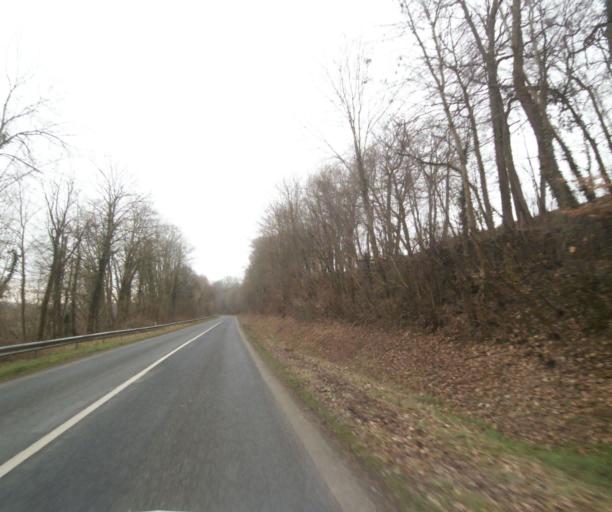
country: FR
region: Champagne-Ardenne
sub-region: Departement de la Haute-Marne
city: Bienville
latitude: 48.5602
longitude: 5.0560
